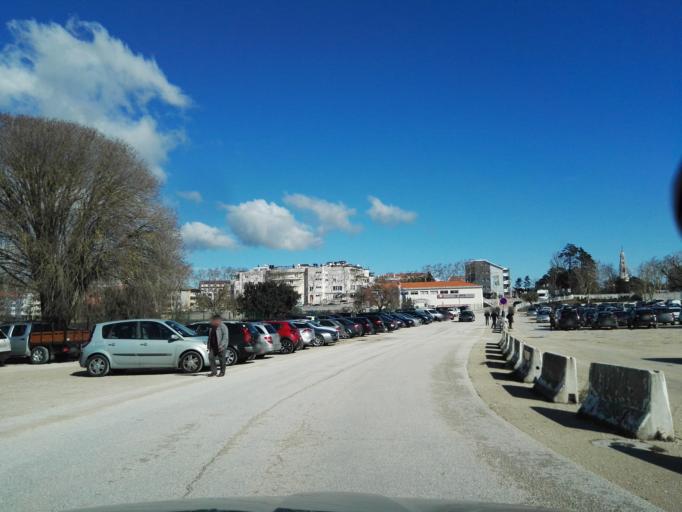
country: PT
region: Santarem
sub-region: Ourem
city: Fatima
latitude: 39.6283
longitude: -8.6795
